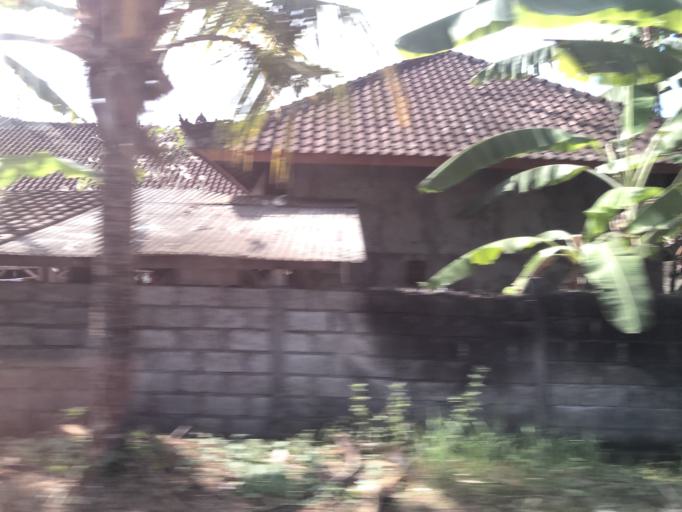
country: ID
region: Bali
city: Banjar Bucu
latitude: -8.5778
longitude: 115.2028
